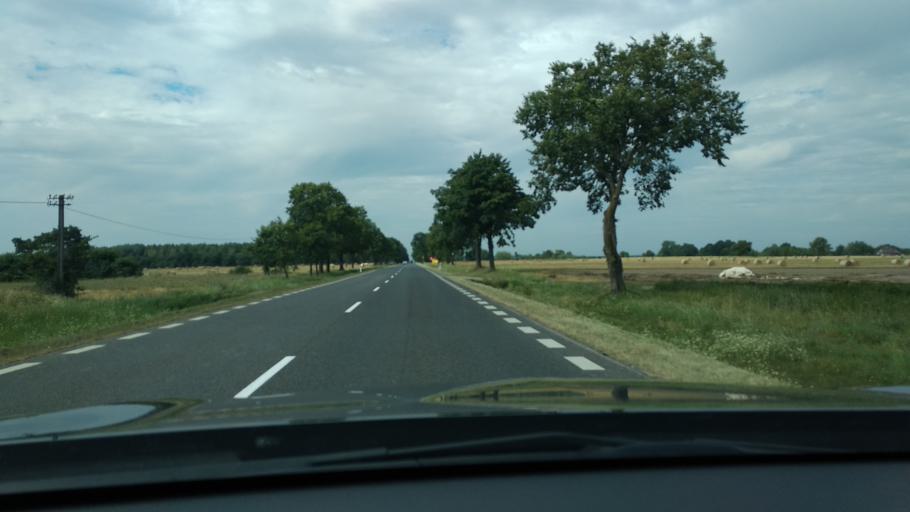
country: PL
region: Masovian Voivodeship
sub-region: Powiat pultuski
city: Zatory
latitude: 52.5489
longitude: 21.1823
